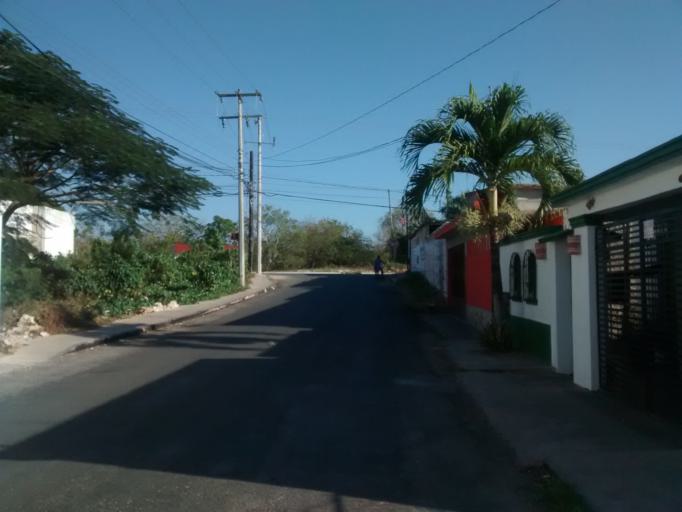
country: MX
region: Yucatan
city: Valladolid
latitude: 20.6892
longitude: -88.1877
